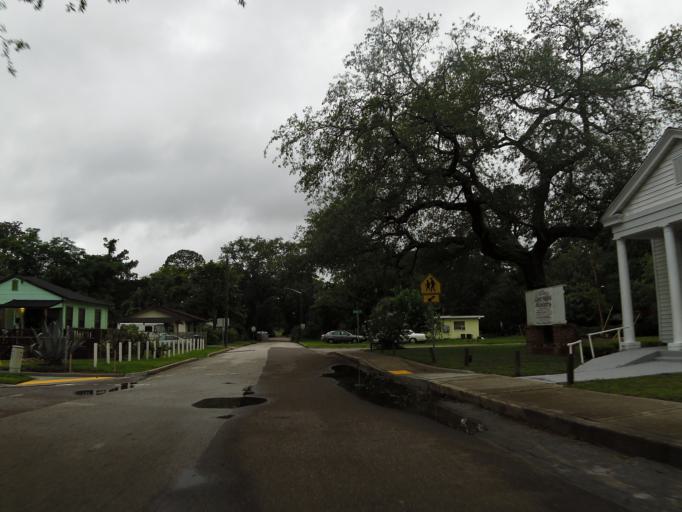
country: US
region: Florida
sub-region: Duval County
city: Jacksonville
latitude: 30.3463
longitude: -81.6327
